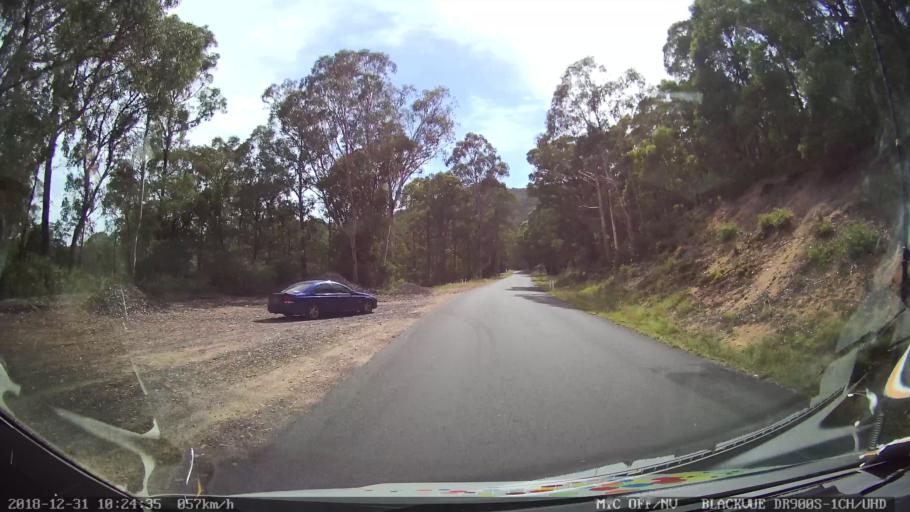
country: AU
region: New South Wales
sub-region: Snowy River
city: Jindabyne
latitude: -36.5117
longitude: 148.1414
